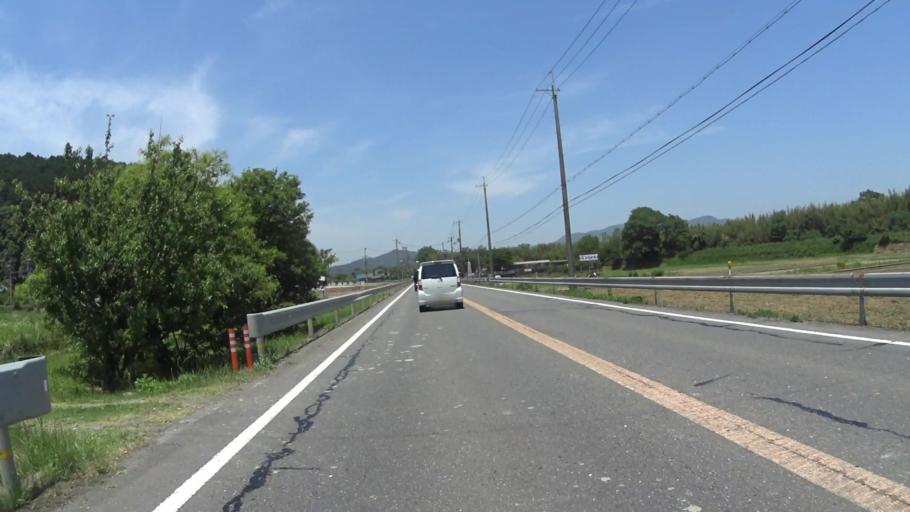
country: JP
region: Kyoto
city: Kameoka
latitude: 35.0593
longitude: 135.5468
